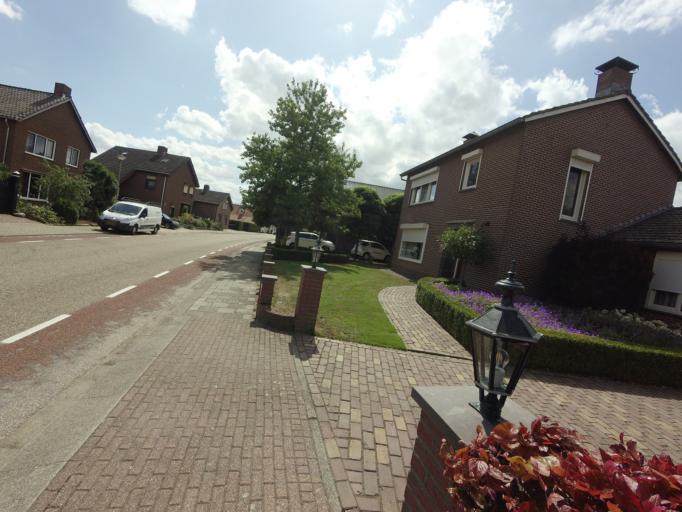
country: NL
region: Limburg
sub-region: Gemeente Maasgouw
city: Maasbracht
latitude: 51.1341
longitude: 5.8607
